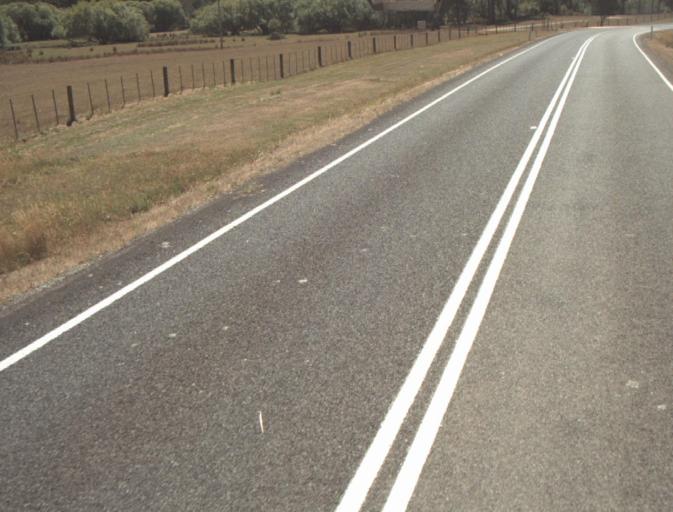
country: AU
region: Tasmania
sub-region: Dorset
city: Scottsdale
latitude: -41.3028
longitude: 147.3817
